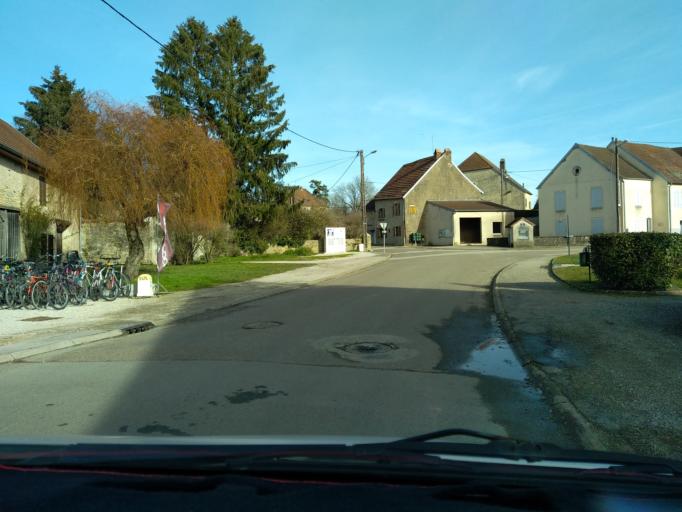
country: FR
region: Franche-Comte
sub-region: Departement de la Haute-Saone
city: Marnay
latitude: 47.3204
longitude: 5.6834
